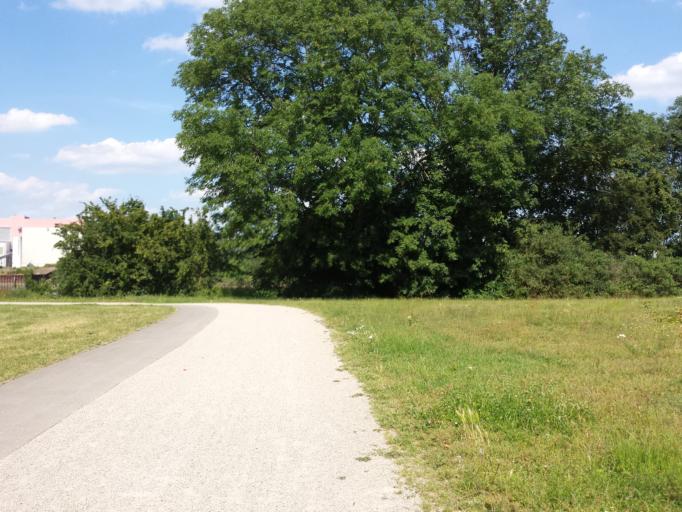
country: DE
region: Bremen
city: Bremen
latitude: 53.0874
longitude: 8.7653
